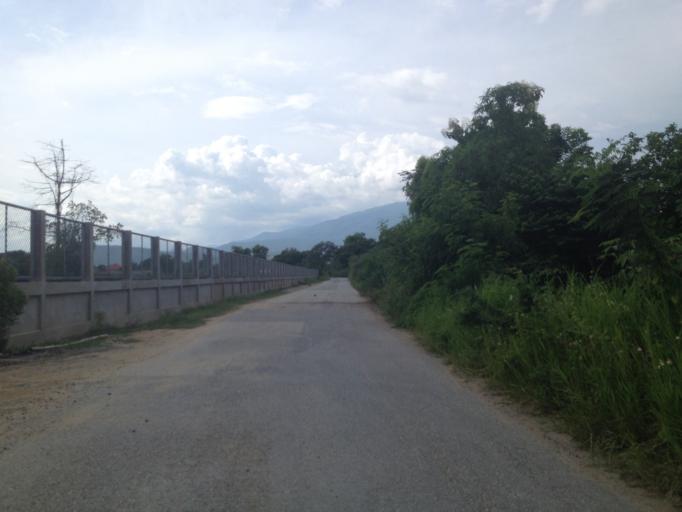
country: TH
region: Chiang Mai
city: Hang Dong
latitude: 18.7174
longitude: 98.9350
